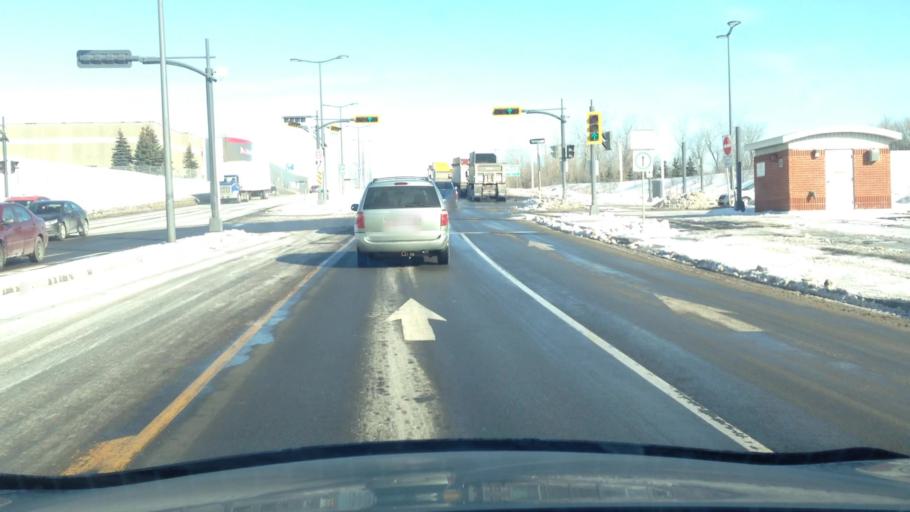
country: CA
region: Quebec
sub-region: Laval
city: Laval
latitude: 45.5528
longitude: -73.7249
